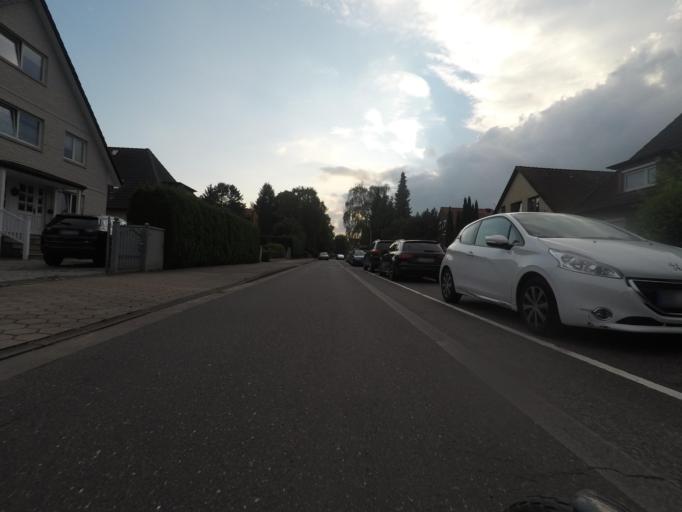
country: DE
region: Hamburg
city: Wandsbek
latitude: 53.5722
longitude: 10.1299
